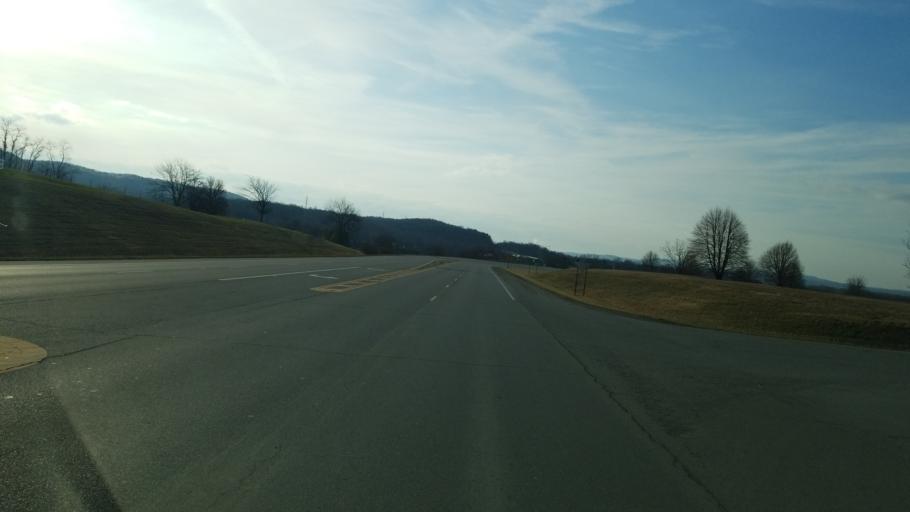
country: US
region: Ohio
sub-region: Ross County
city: Chillicothe
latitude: 39.3925
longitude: -82.9680
